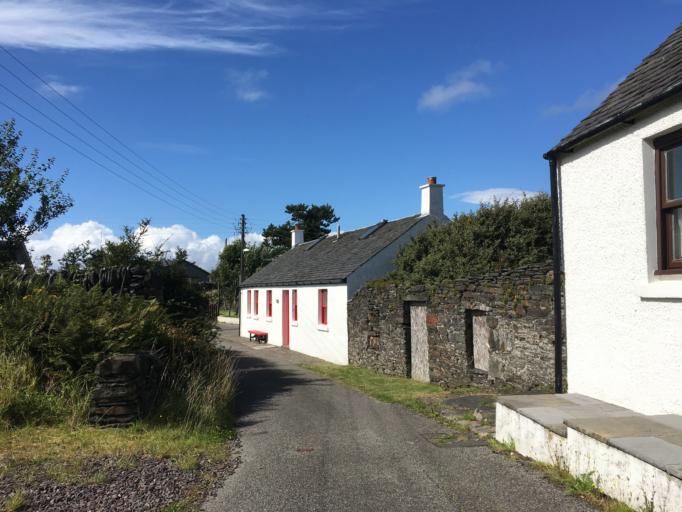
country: GB
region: Scotland
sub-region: Argyll and Bute
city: Isle Of Mull
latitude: 56.2566
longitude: -5.6507
